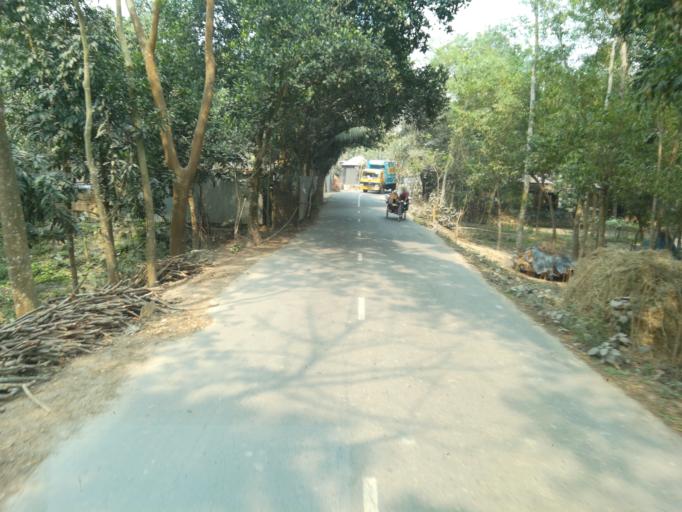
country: BD
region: Dhaka
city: Nagarpur
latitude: 23.9881
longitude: 89.8448
